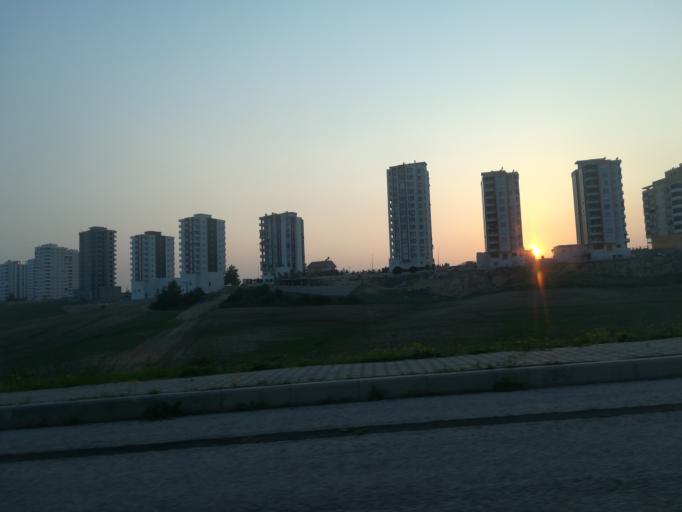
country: TR
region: Adana
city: Adana
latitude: 37.0793
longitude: 35.4125
